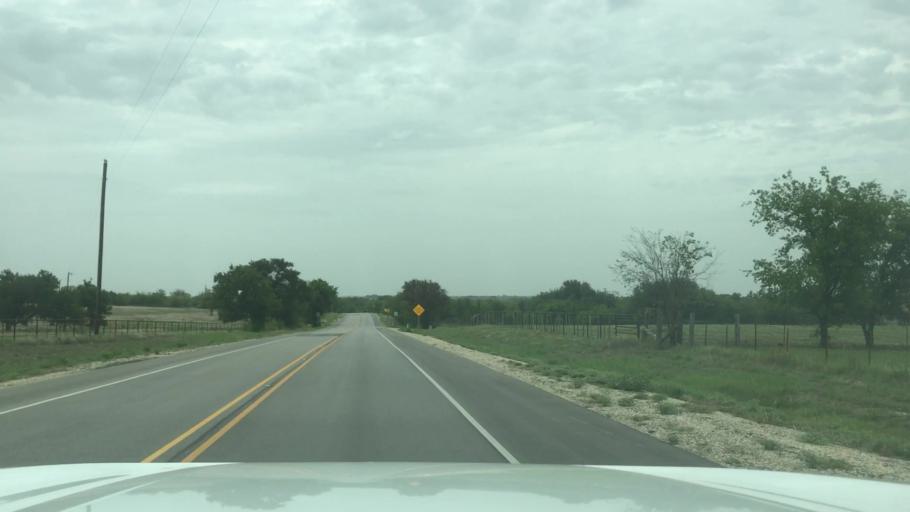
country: US
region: Texas
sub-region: Erath County
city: Dublin
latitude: 32.0635
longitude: -98.2144
